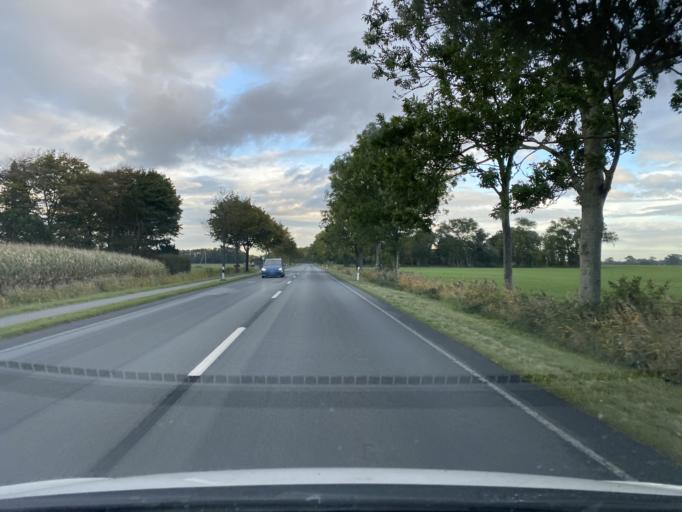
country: DE
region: Lower Saxony
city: Nordleda
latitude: 53.8013
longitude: 8.8298
